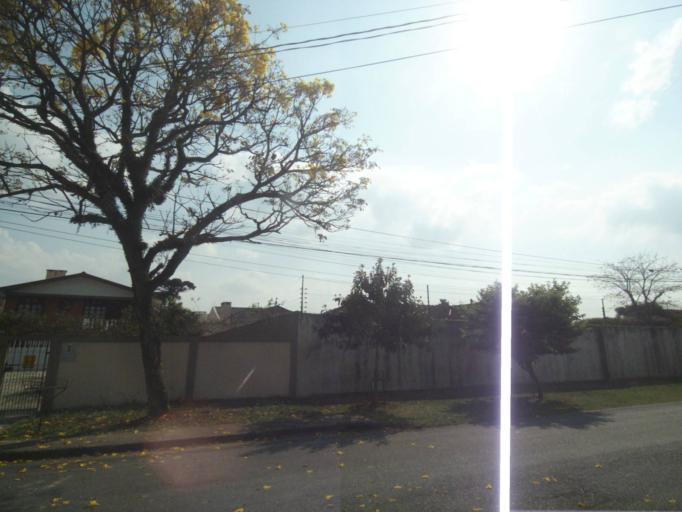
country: BR
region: Parana
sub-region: Sao Jose Dos Pinhais
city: Sao Jose dos Pinhais
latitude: -25.5050
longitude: -49.2544
